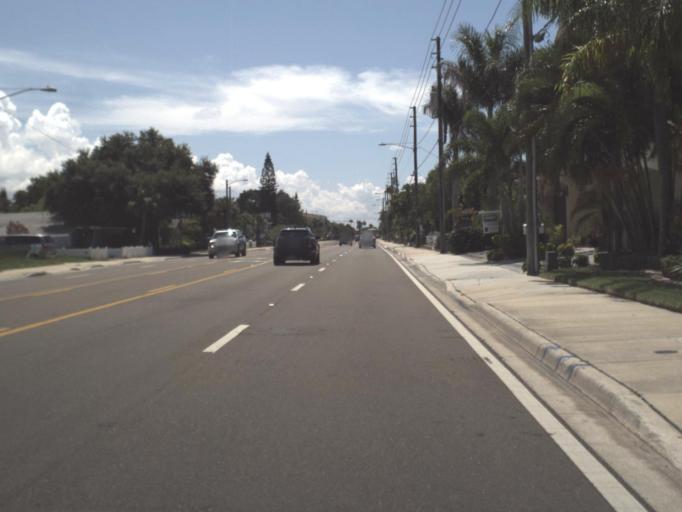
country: US
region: Florida
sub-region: Pinellas County
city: Redington Beach
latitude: 27.8075
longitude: -82.8101
